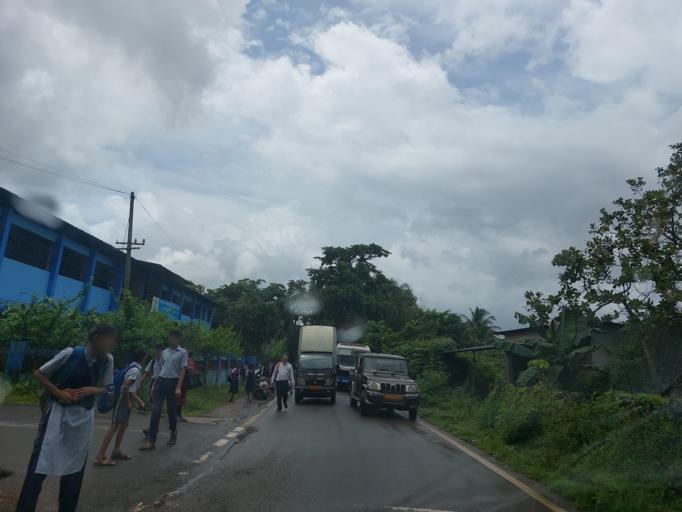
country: IN
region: Goa
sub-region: North Goa
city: Valpoy
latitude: 15.5407
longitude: 74.1371
